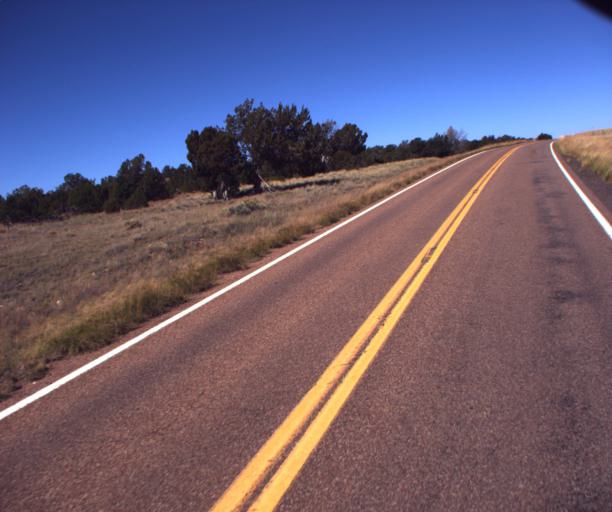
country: US
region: Arizona
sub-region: Navajo County
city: Heber-Overgaard
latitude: 34.4550
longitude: -110.4632
